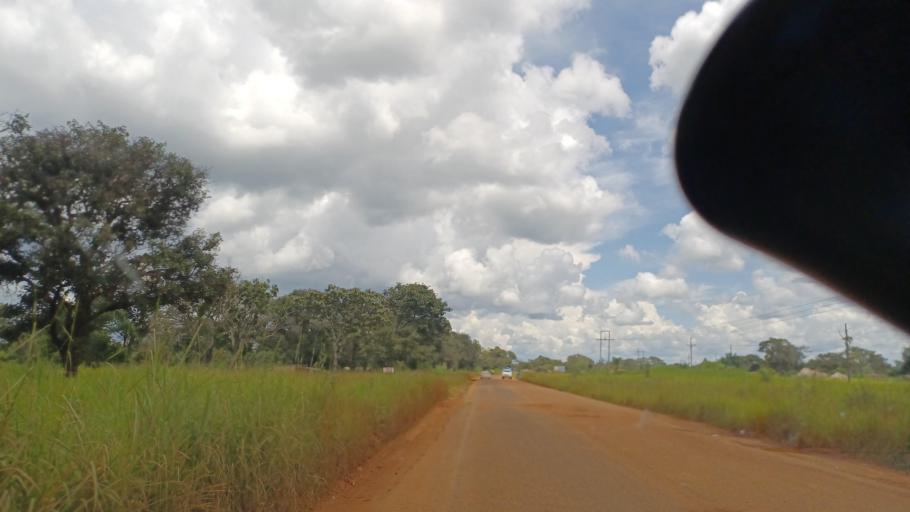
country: ZM
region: North-Western
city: Solwezi
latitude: -12.4795
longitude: 26.1983
